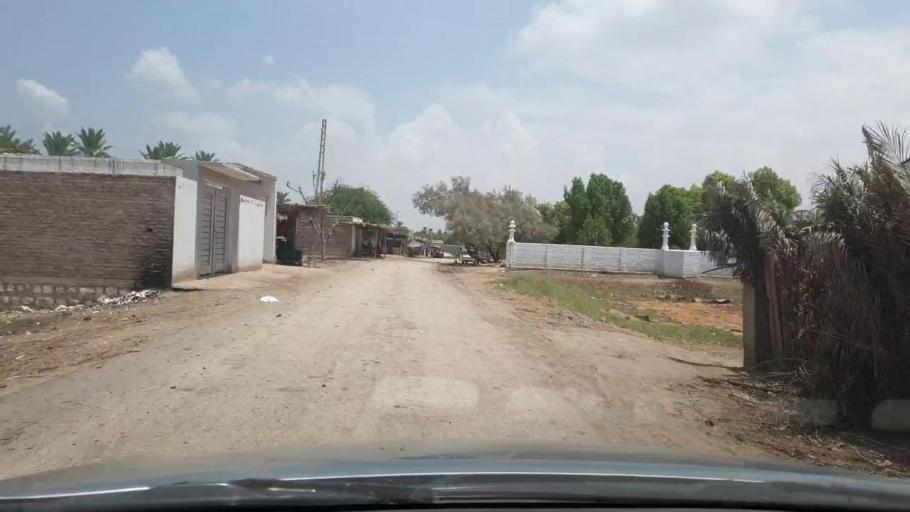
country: PK
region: Sindh
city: Khairpur
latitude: 27.4364
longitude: 68.7650
